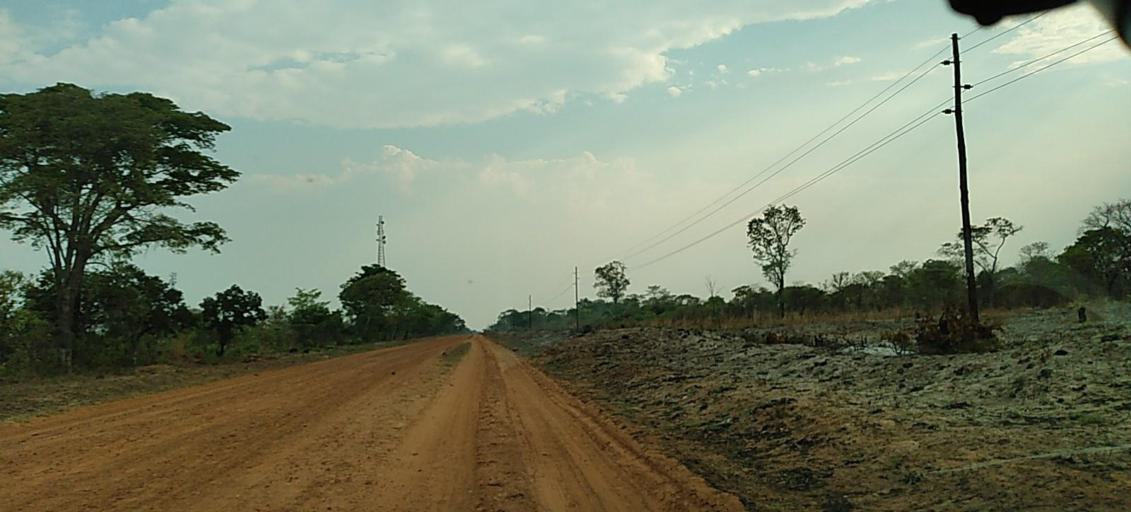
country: ZM
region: North-Western
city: Kabompo
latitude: -13.8817
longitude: 23.6635
